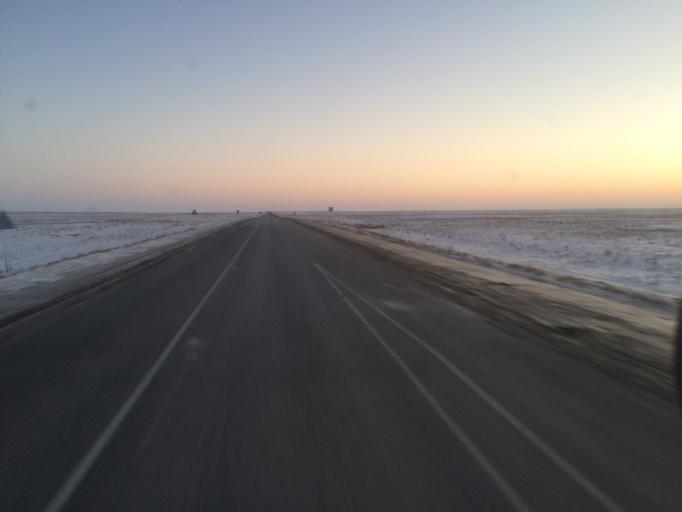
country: KZ
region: Qyzylorda
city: Sekseuil
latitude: 47.2932
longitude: 61.5341
